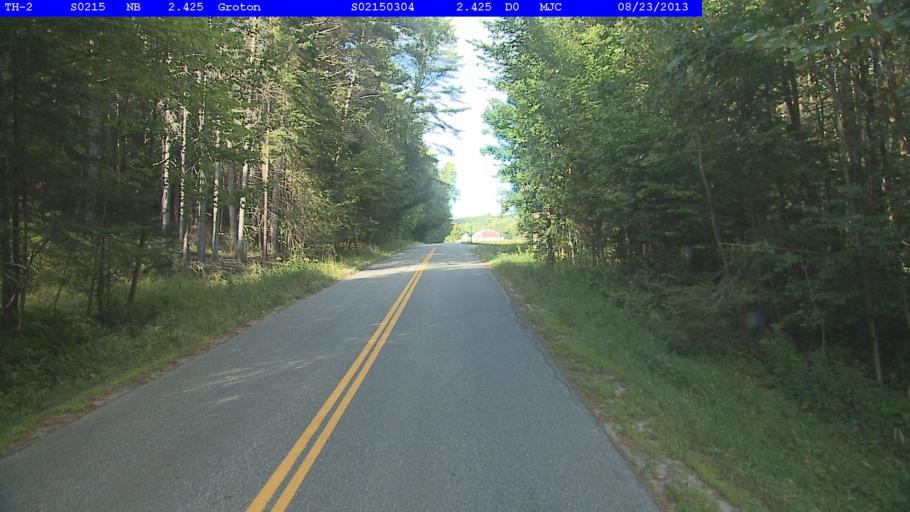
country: US
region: New Hampshire
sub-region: Grafton County
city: Woodsville
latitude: 44.2422
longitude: -72.1815
